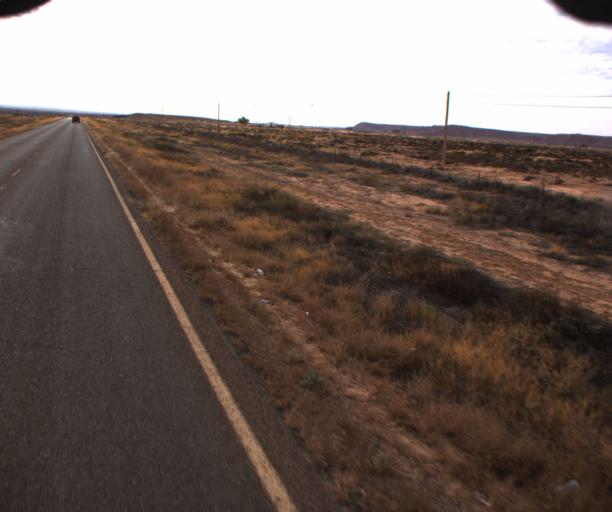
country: US
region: Arizona
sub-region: Apache County
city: Many Farms
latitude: 36.3199
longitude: -109.6159
